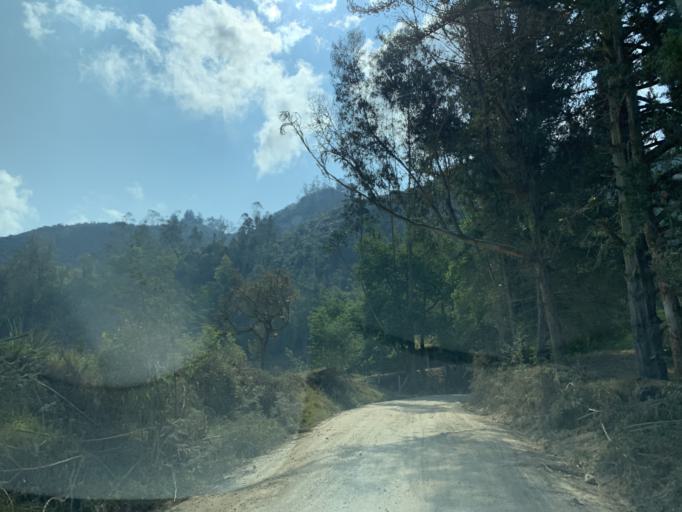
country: CO
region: Boyaca
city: Turmeque
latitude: 5.2937
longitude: -73.5008
